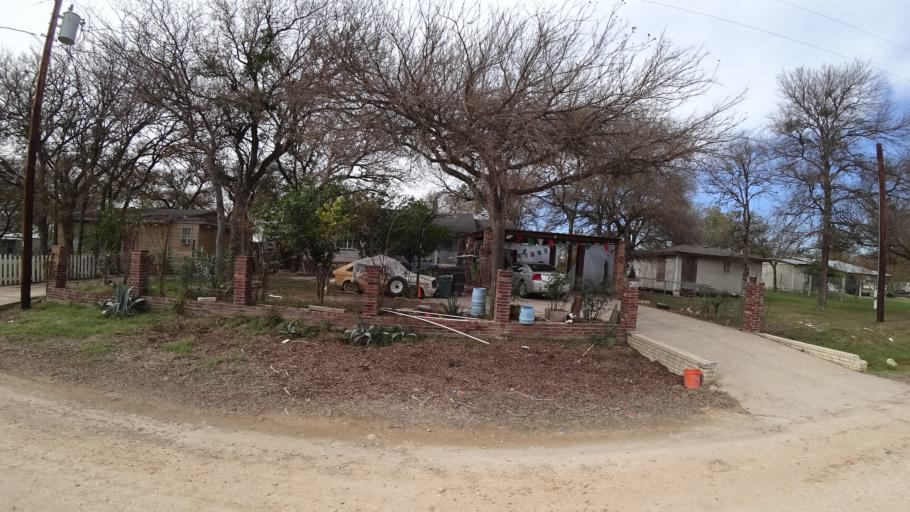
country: US
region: Texas
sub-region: Travis County
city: Garfield
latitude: 30.1346
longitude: -97.5706
